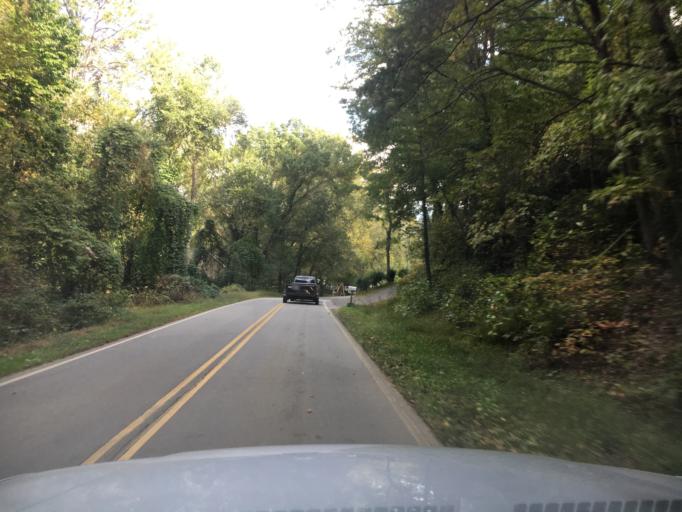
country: US
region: North Carolina
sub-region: Buncombe County
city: Swannanoa
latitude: 35.6000
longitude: -82.4338
